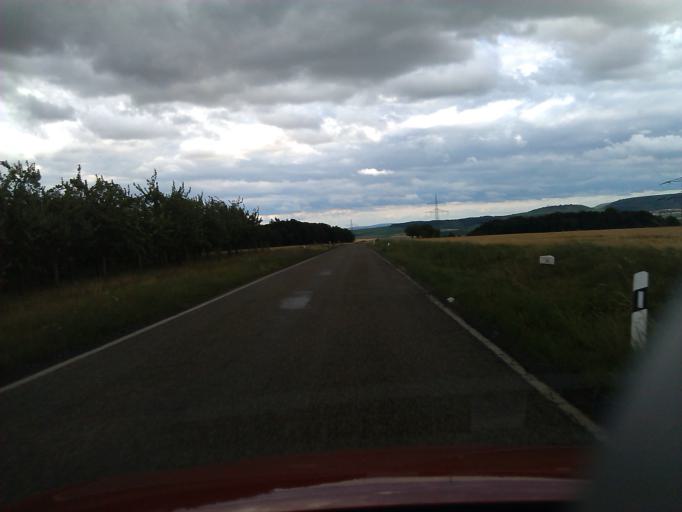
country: DE
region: Baden-Wuerttemberg
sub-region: Regierungsbezirk Stuttgart
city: Guglingen
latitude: 49.0869
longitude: 8.9927
